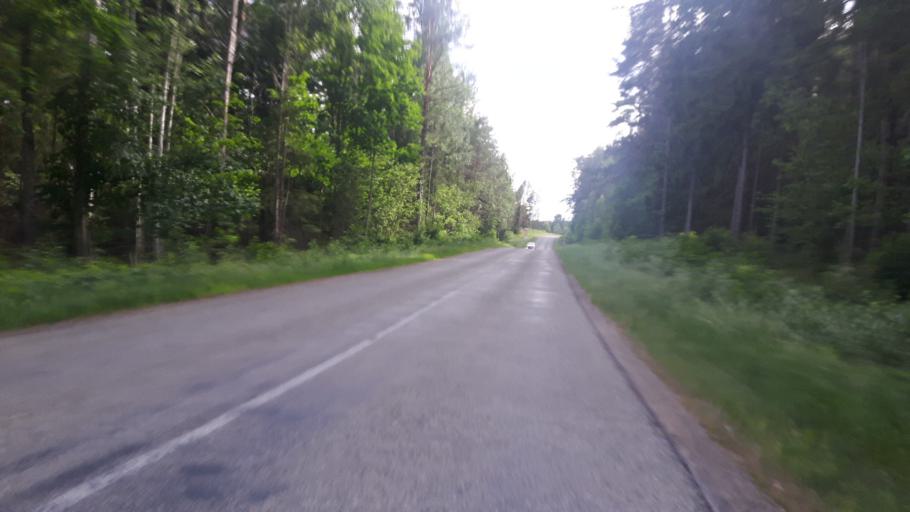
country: LV
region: Engure
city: Smarde
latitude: 56.9878
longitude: 23.2930
